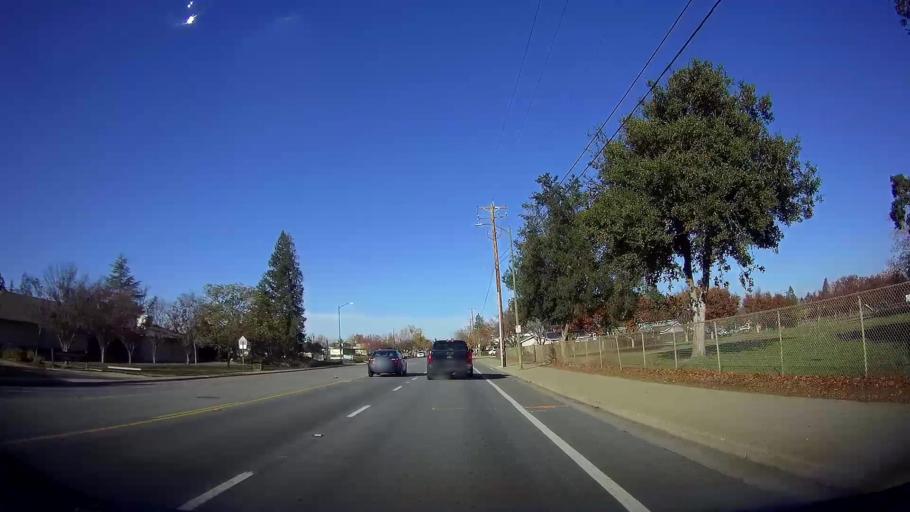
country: US
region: California
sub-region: Santa Clara County
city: Cambrian Park
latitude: 37.2655
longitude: -121.9313
